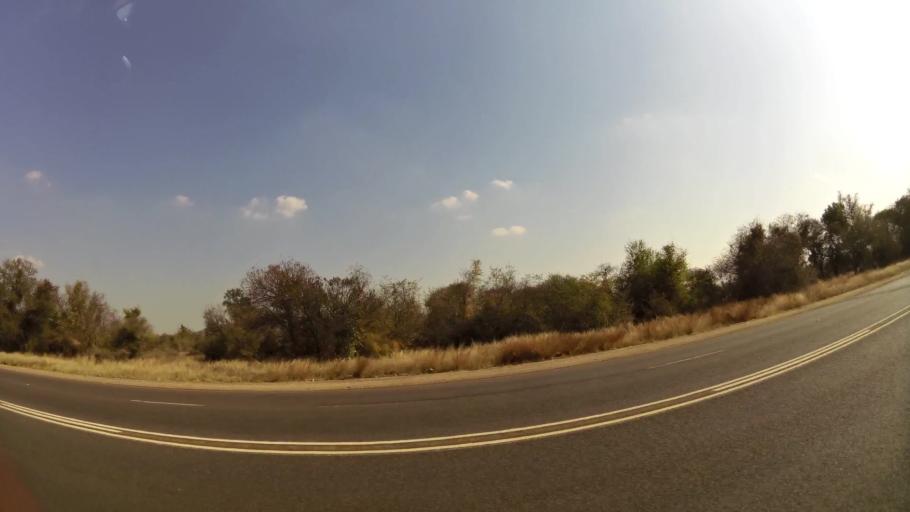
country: ZA
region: North-West
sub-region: Bojanala Platinum District Municipality
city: Mogwase
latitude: -25.4254
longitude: 27.0805
